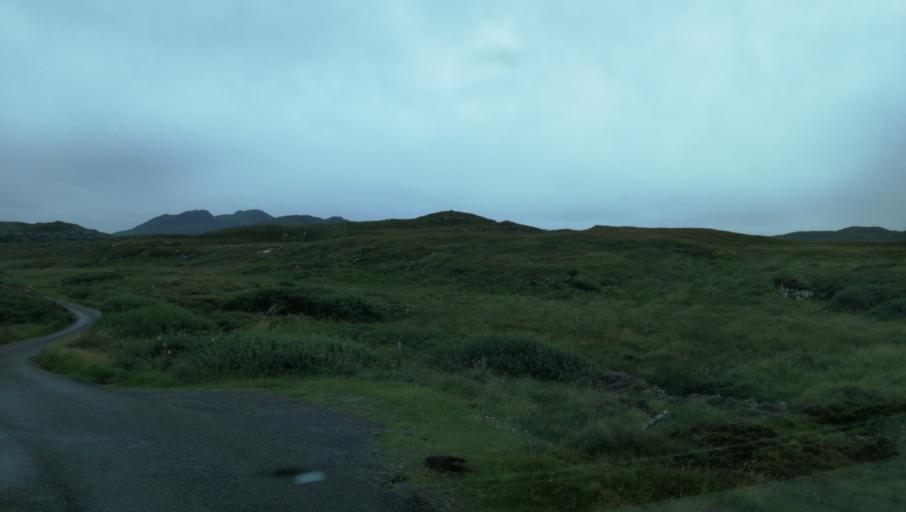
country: GB
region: Scotland
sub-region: Argyll and Bute
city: Isle Of Mull
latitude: 56.7222
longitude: -6.2190
